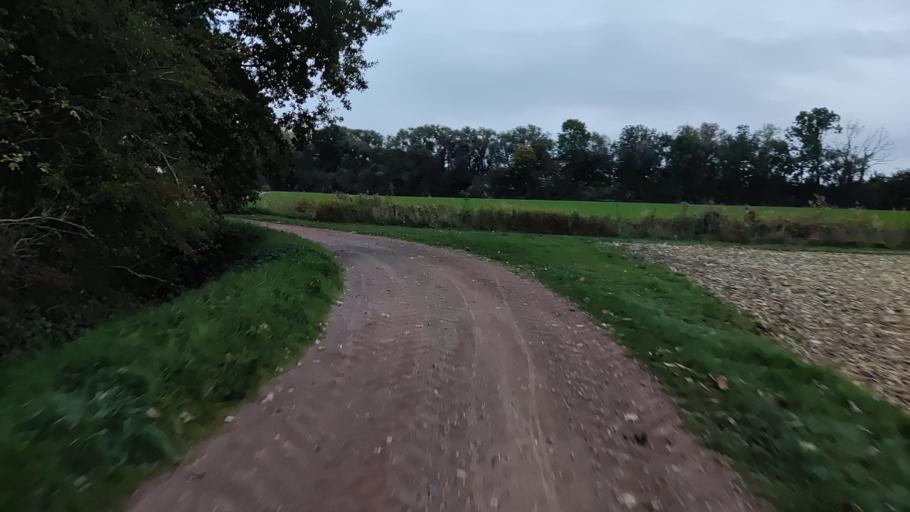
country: BE
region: Flanders
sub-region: Provincie Vlaams-Brabant
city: Tienen
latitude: 50.7879
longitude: 4.9213
